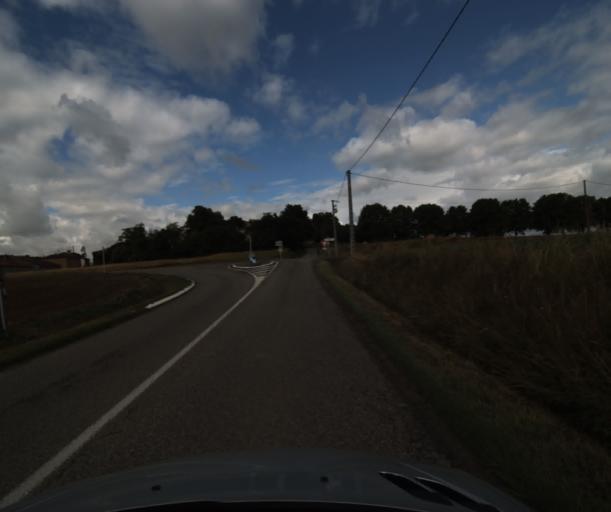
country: FR
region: Midi-Pyrenees
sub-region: Departement du Tarn-et-Garonne
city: Saint-Nicolas-de-la-Grave
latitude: 44.0192
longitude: 1.0048
